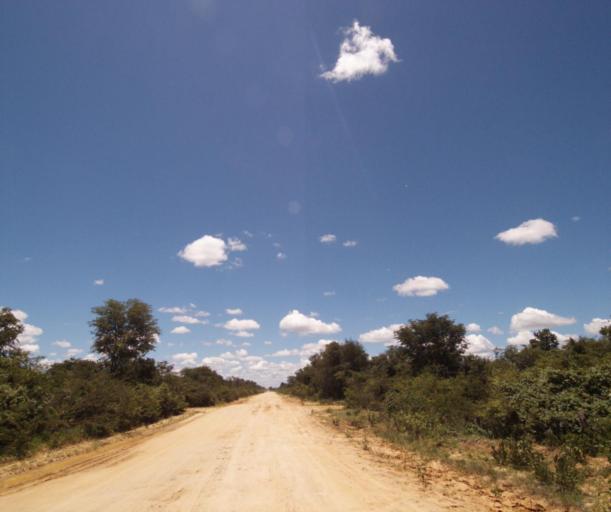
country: BR
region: Bahia
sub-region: Carinhanha
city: Carinhanha
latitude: -14.2294
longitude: -43.8665
